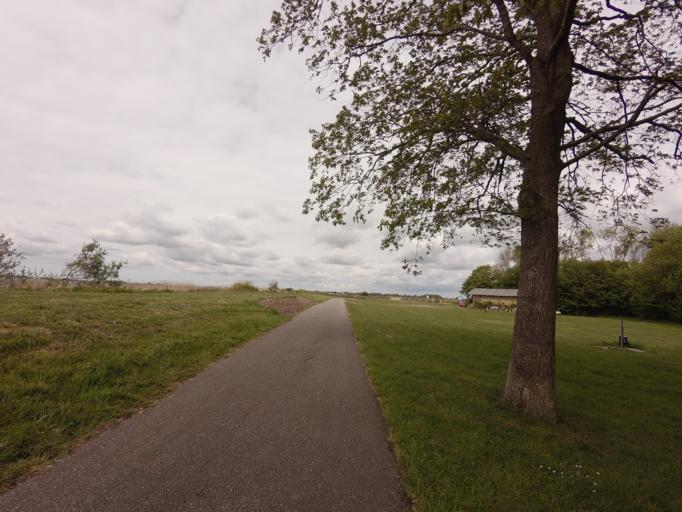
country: NL
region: Friesland
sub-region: Sudwest Fryslan
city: Heeg
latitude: 52.9469
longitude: 5.6006
